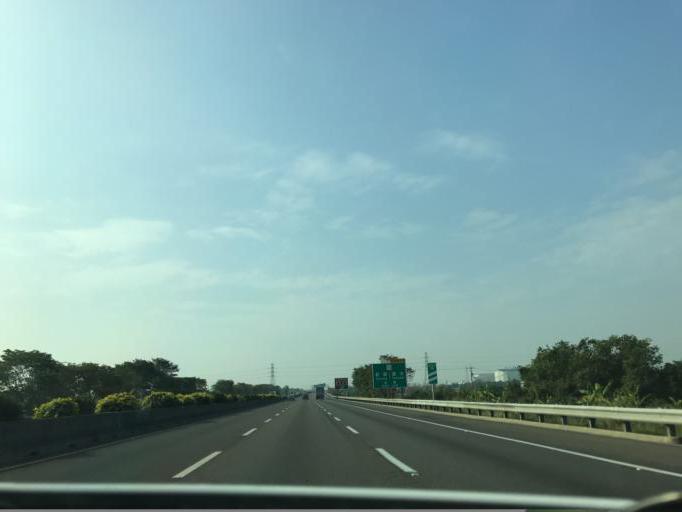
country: TW
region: Taiwan
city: Xinying
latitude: 23.3199
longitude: 120.2981
